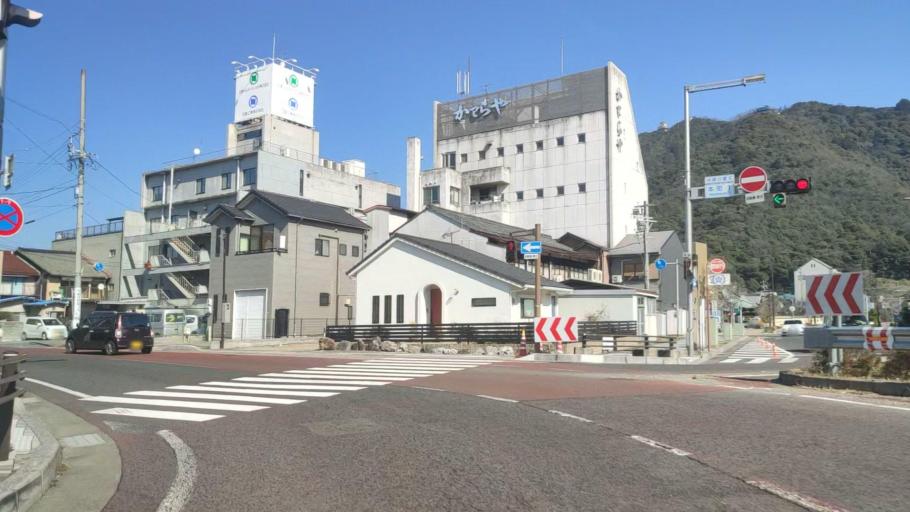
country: JP
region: Gifu
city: Gifu-shi
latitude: 35.4320
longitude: 136.7689
